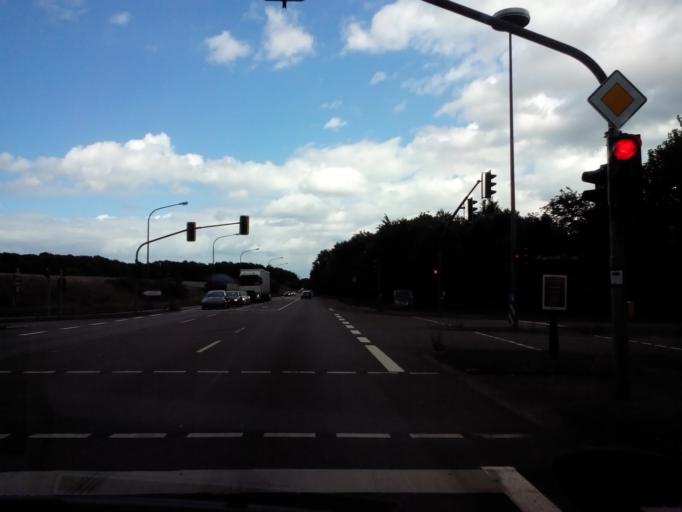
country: DE
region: Saarland
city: Saarlouis
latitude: 49.3016
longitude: 6.7226
